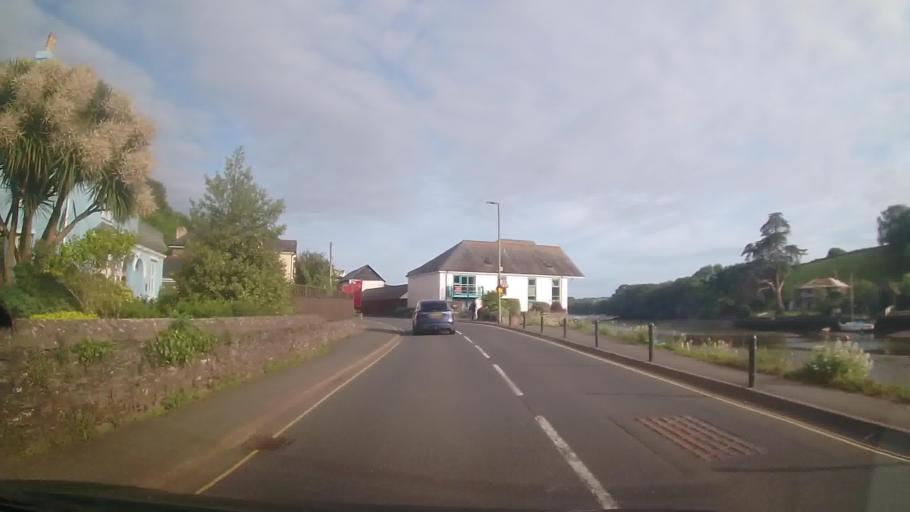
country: GB
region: England
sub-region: Devon
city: Kingsbridge
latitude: 50.2792
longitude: -3.7735
